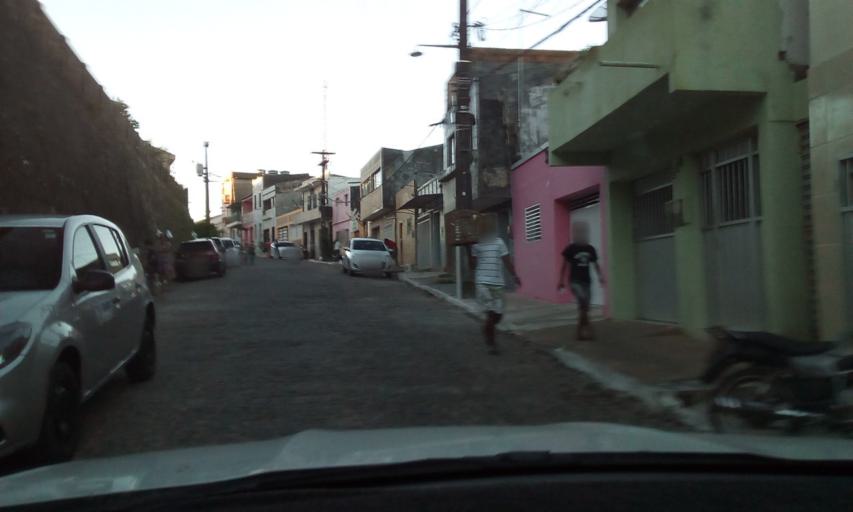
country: BR
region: Paraiba
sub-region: Areia
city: Areia
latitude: -6.9706
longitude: -35.7041
